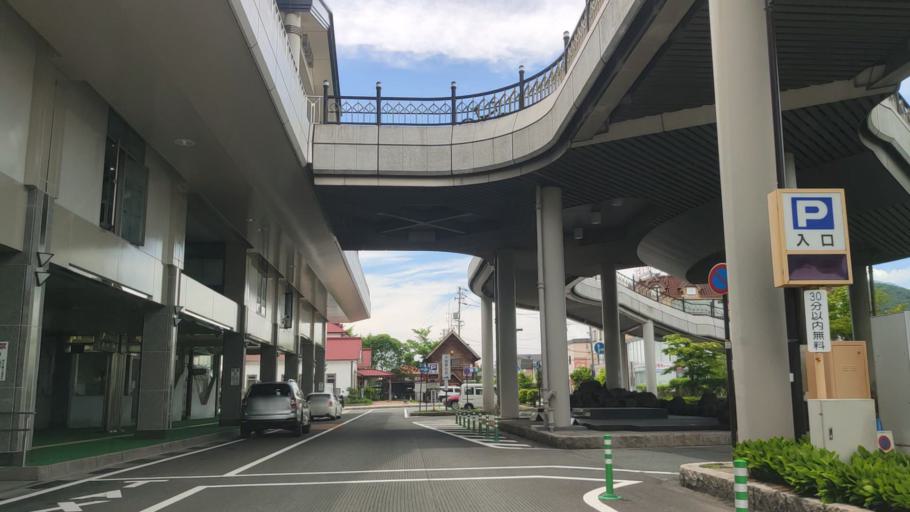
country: JP
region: Nagano
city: Saku
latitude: 36.3431
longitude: 138.6355
